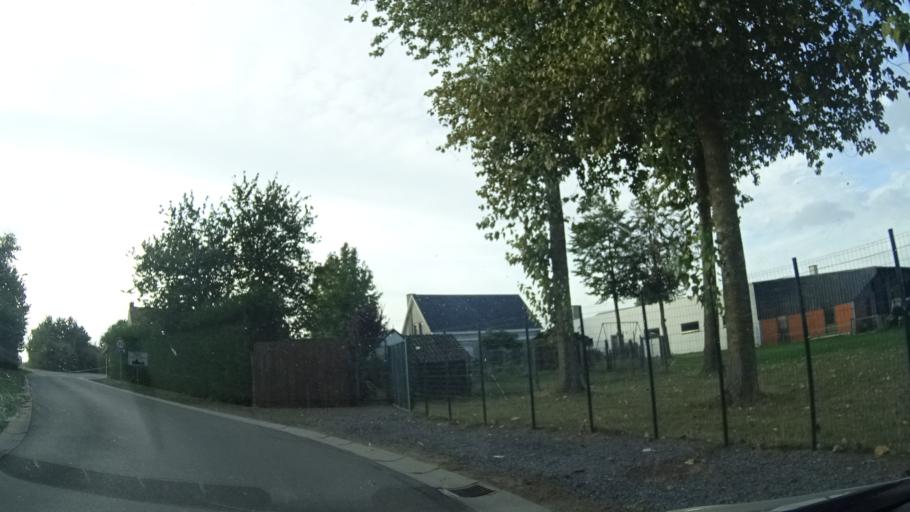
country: BE
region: Wallonia
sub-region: Province du Hainaut
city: Peruwelz
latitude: 50.5766
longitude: 3.5739
